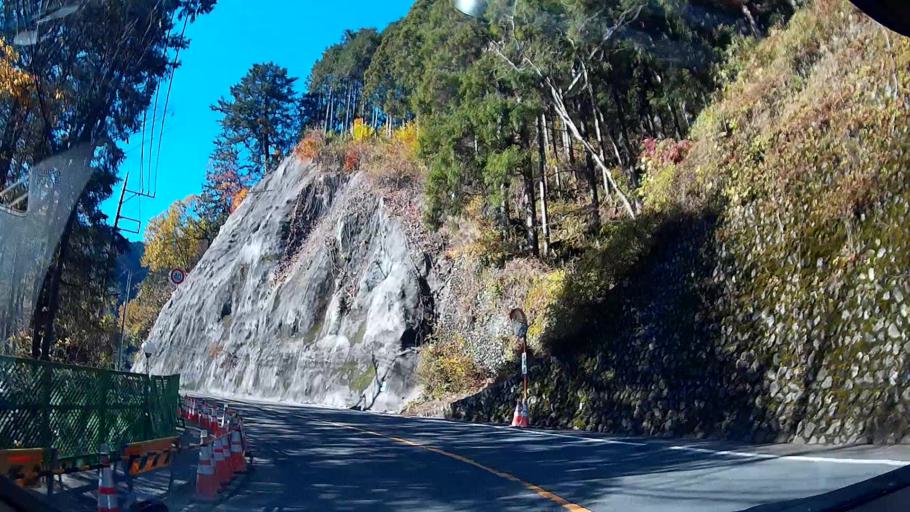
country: JP
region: Tokyo
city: Itsukaichi
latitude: 35.7047
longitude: 139.1436
